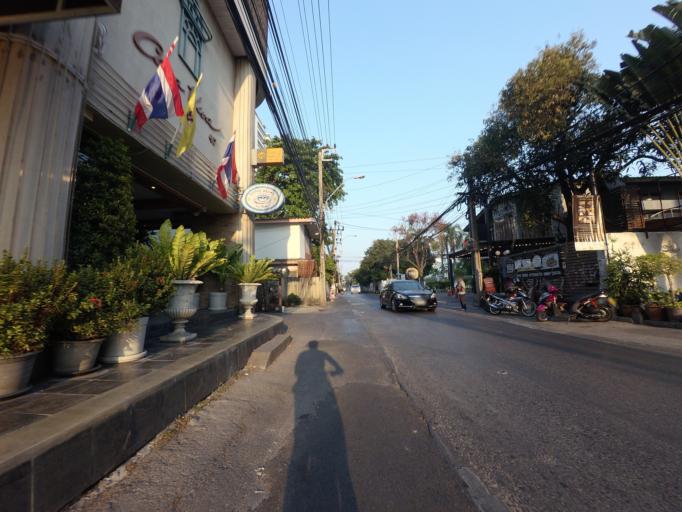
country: TH
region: Bangkok
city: Watthana
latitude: 13.7300
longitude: 100.5909
